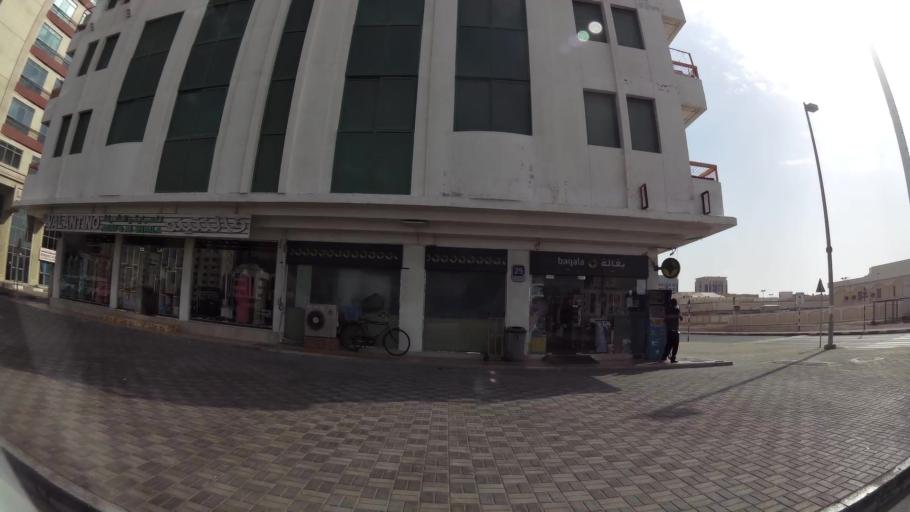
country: AE
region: Abu Dhabi
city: Abu Dhabi
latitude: 24.3204
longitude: 54.5356
